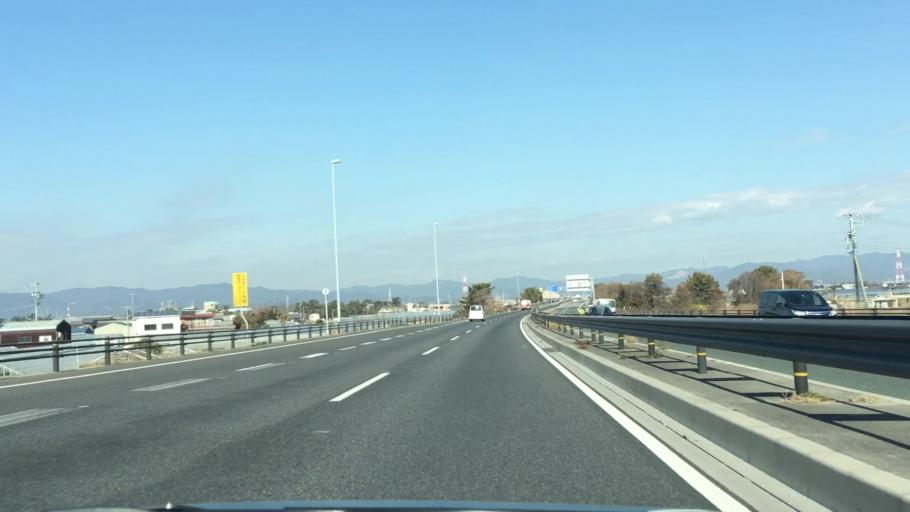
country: JP
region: Aichi
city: Kozakai-cho
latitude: 34.7643
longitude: 137.3322
